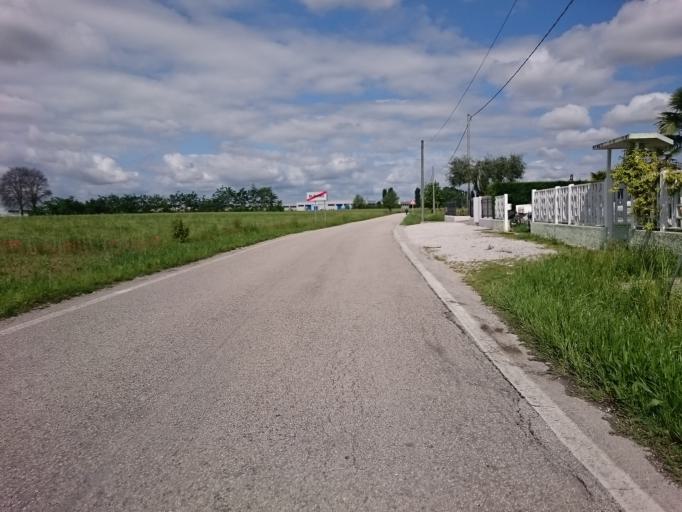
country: IT
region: Veneto
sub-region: Provincia di Padova
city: Rubano
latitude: 45.4364
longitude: 11.7817
